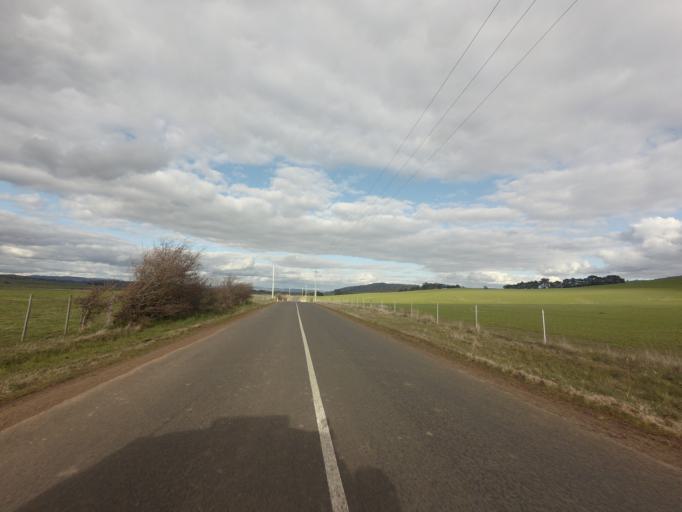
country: AU
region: Tasmania
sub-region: Northern Midlands
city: Evandale
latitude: -41.8921
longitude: 147.3335
